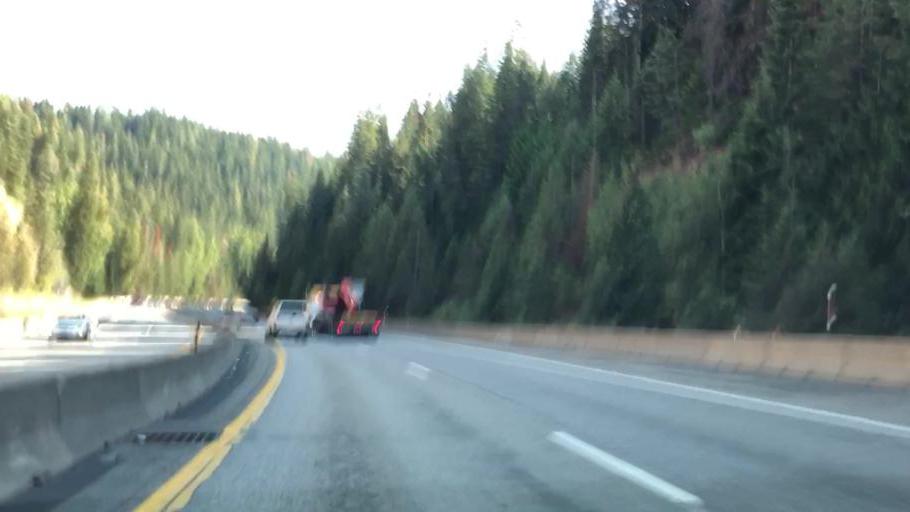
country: US
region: Idaho
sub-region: Shoshone County
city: Pinehurst
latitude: 47.5991
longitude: -116.4961
